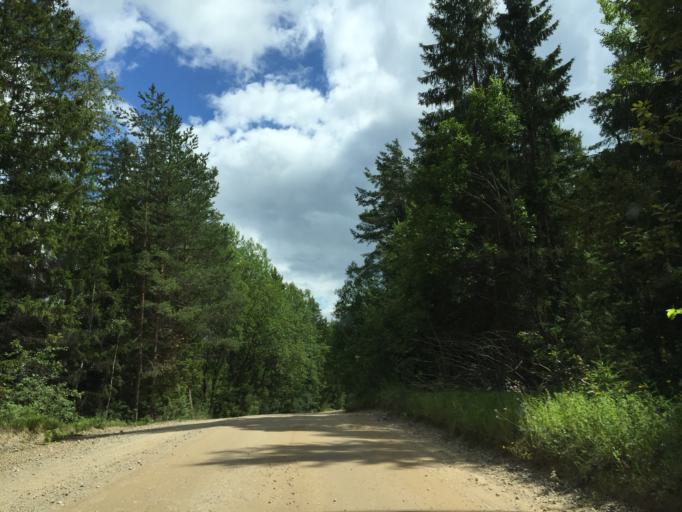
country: LV
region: Ropazu
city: Ropazi
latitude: 56.9145
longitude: 24.7505
